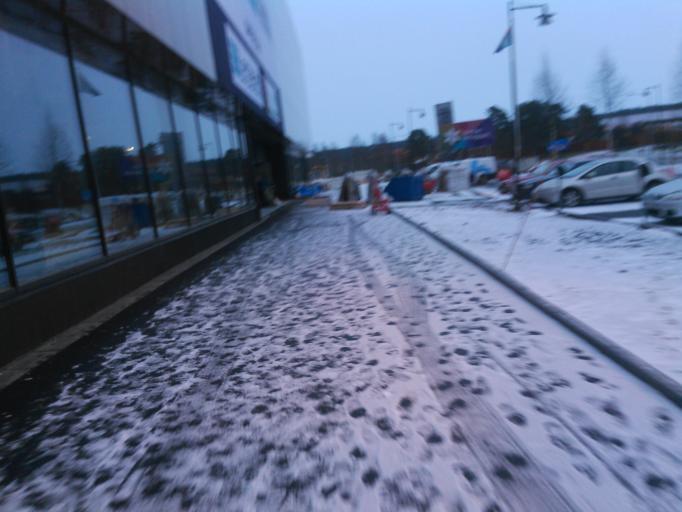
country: SE
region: Vaesterbotten
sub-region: Umea Kommun
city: Umea
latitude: 63.8344
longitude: 20.2645
